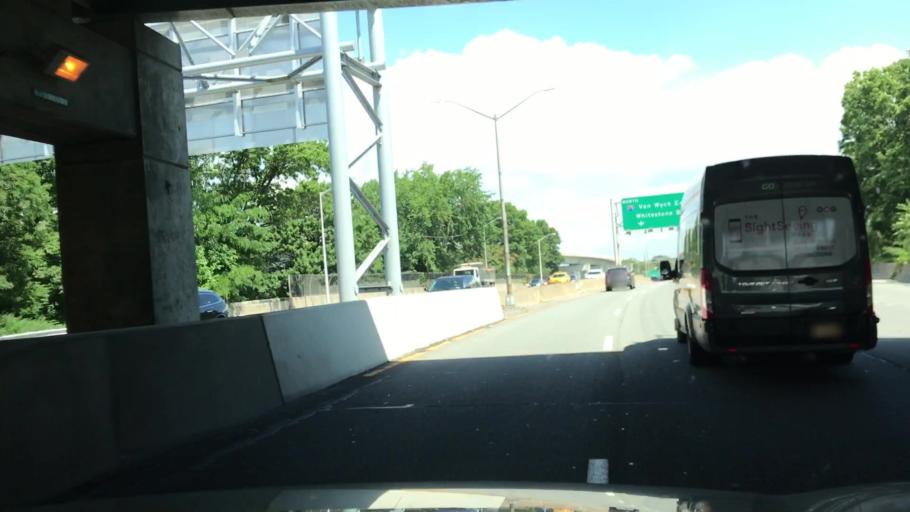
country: US
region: New York
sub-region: Queens County
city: Jamaica
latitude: 40.6649
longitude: -73.8011
